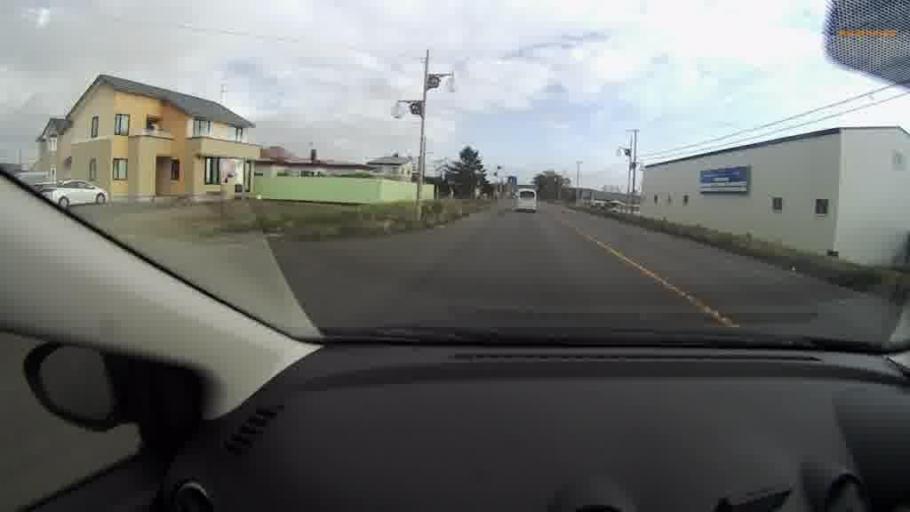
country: JP
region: Hokkaido
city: Kushiro
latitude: 42.9765
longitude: 144.1318
